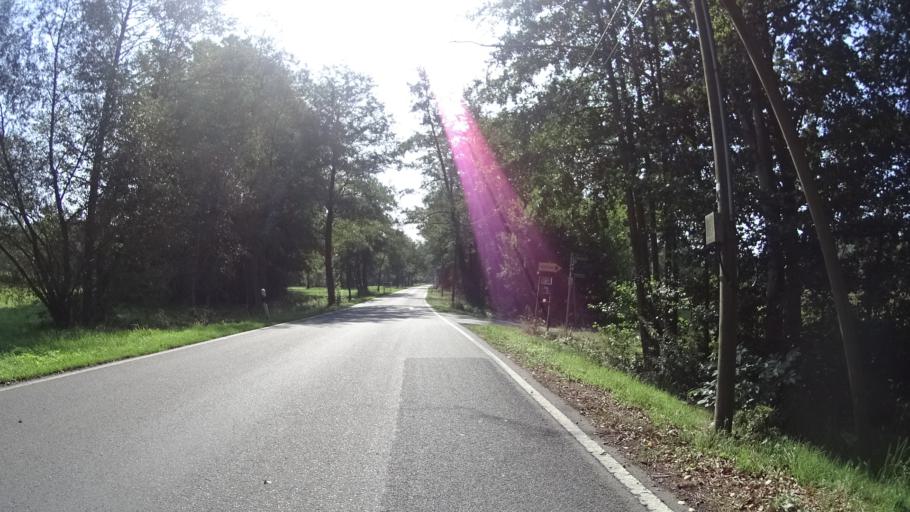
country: DE
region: Brandenburg
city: Burg
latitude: 51.8591
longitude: 14.1267
